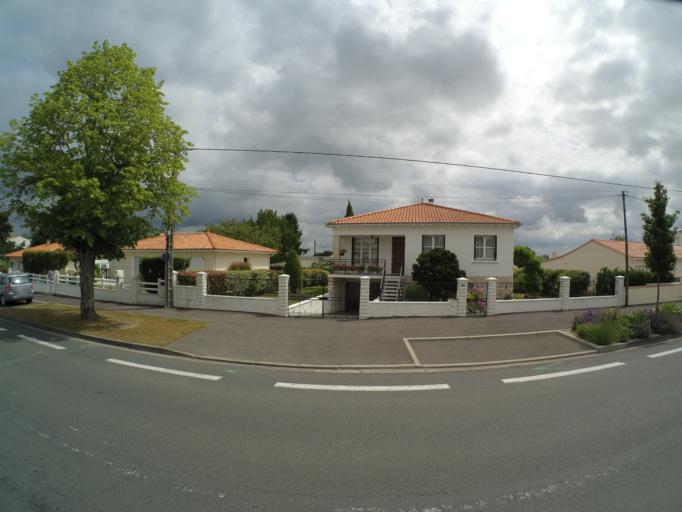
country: FR
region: Poitou-Charentes
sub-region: Departement de la Charente-Maritime
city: Rochefort
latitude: 45.9521
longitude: -0.9685
